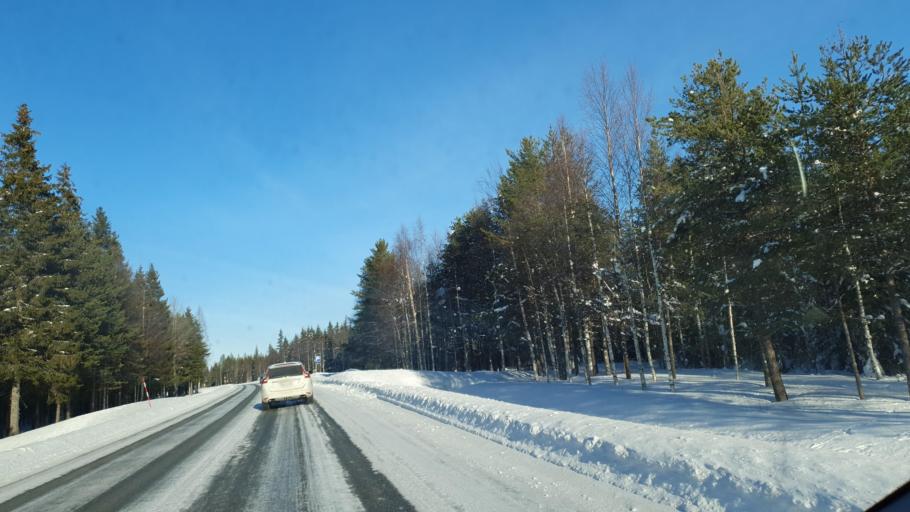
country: SE
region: Norrbotten
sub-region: Overtornea Kommun
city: OEvertornea
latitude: 66.4821
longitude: 23.7374
